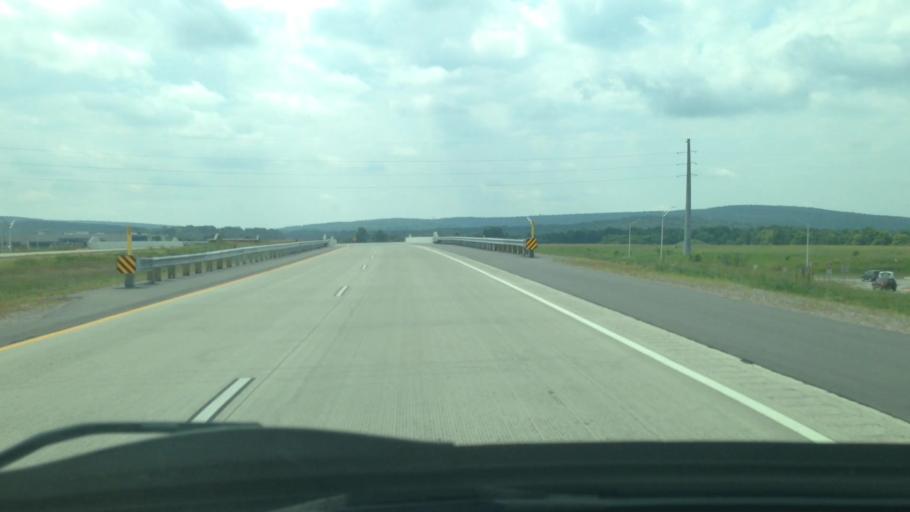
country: US
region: Wisconsin
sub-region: Sauk County
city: West Baraboo
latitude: 43.4614
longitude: -89.7781
